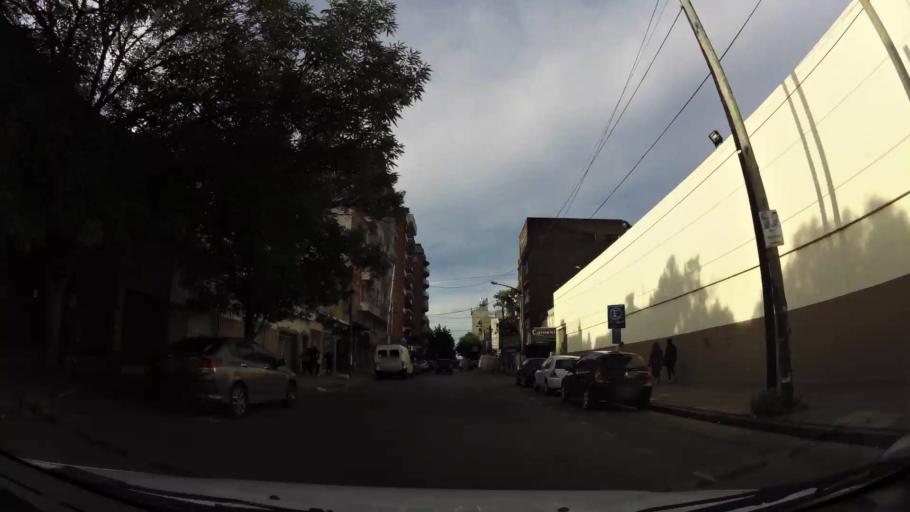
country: AR
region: Buenos Aires
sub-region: Partido de Moron
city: Moron
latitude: -34.6537
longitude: -58.6212
